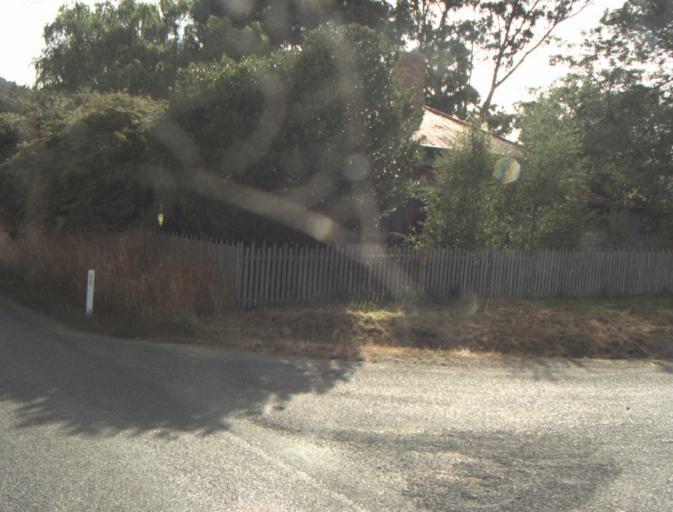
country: AU
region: Tasmania
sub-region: Launceston
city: Mayfield
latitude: -41.1778
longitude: 147.2272
